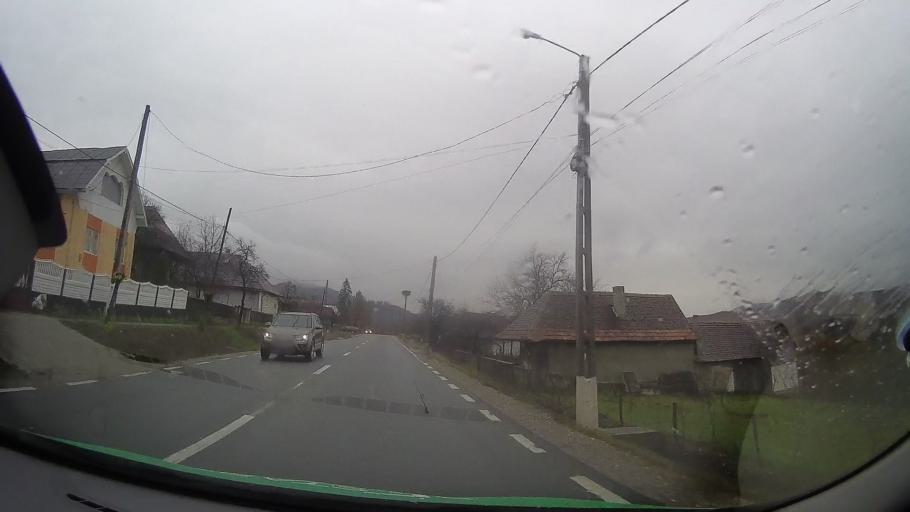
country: RO
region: Bistrita-Nasaud
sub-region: Comuna Galatii Bistritei
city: Galatii Bistritei
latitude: 46.9871
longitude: 24.4253
